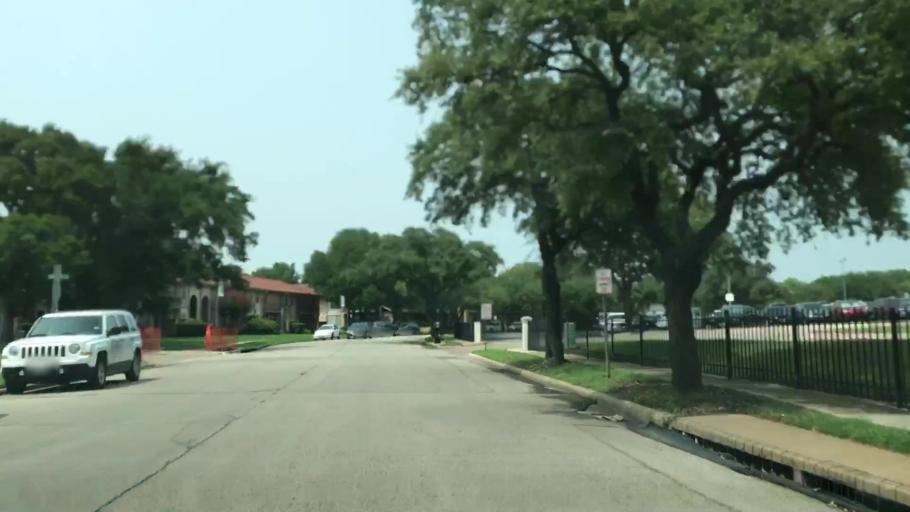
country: US
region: Texas
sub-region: Dallas County
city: Irving
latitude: 32.8518
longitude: -96.9616
